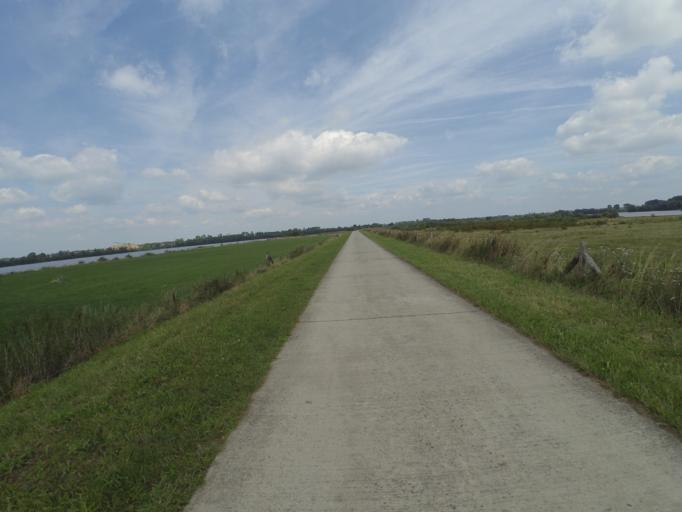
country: NL
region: Limburg
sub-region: Gemeente Stein
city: Berg
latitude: 51.0512
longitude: 5.7585
